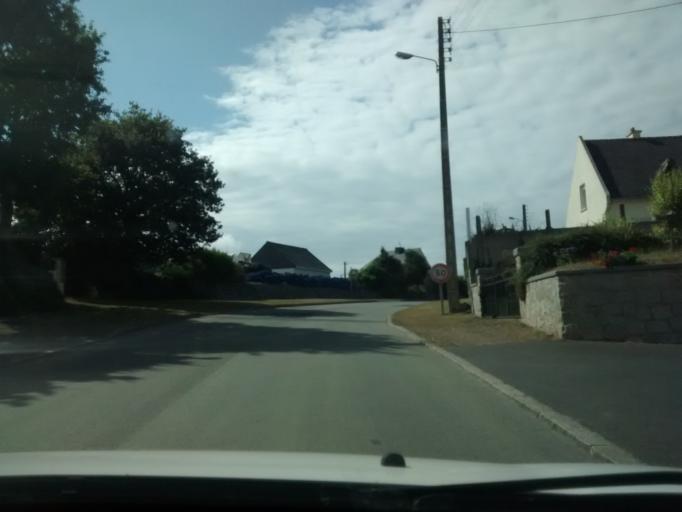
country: FR
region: Brittany
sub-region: Departement des Cotes-d'Armor
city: Penvenan
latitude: 48.8034
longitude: -3.2910
